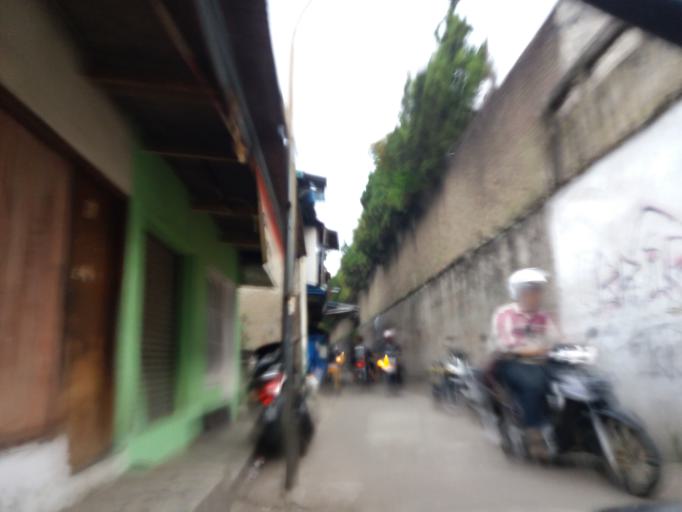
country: ID
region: West Java
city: Bandung
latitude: -6.9058
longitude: 107.6526
